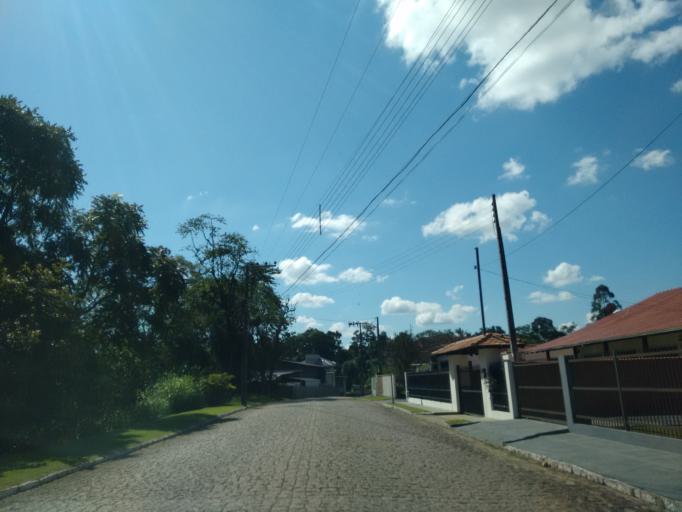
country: BR
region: Santa Catarina
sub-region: Indaial
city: Indaial
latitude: -26.8958
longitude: -49.1919
